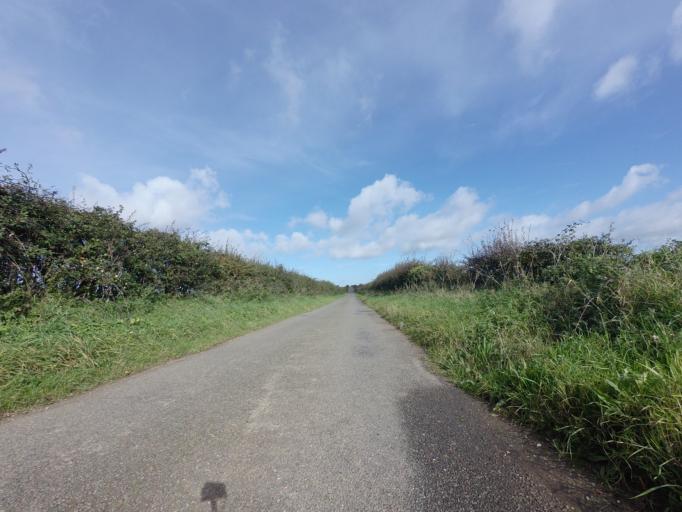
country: GB
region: England
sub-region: Norfolk
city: Wells-next-the-Sea
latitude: 52.9269
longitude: 0.7233
